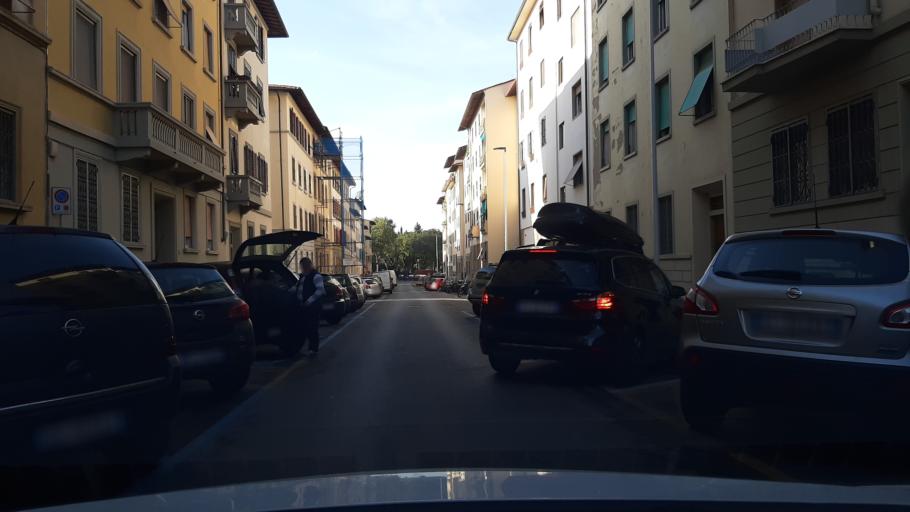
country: IT
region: Tuscany
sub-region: Province of Florence
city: Fiesole
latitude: 43.7814
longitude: 11.2895
